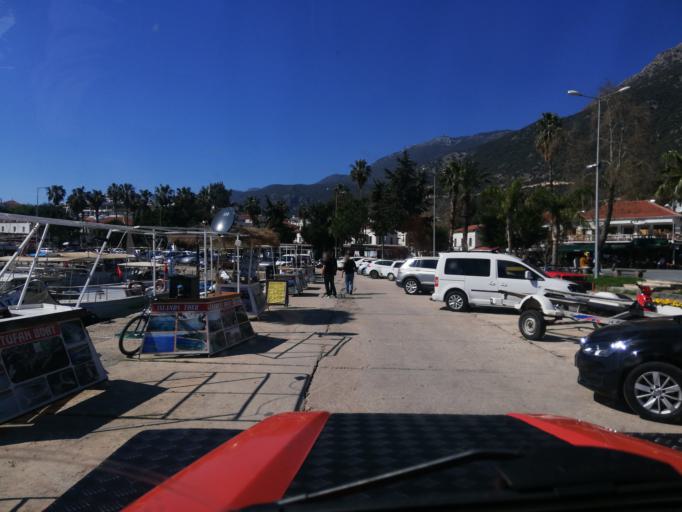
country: TR
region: Antalya
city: Kas
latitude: 36.1988
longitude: 29.6416
